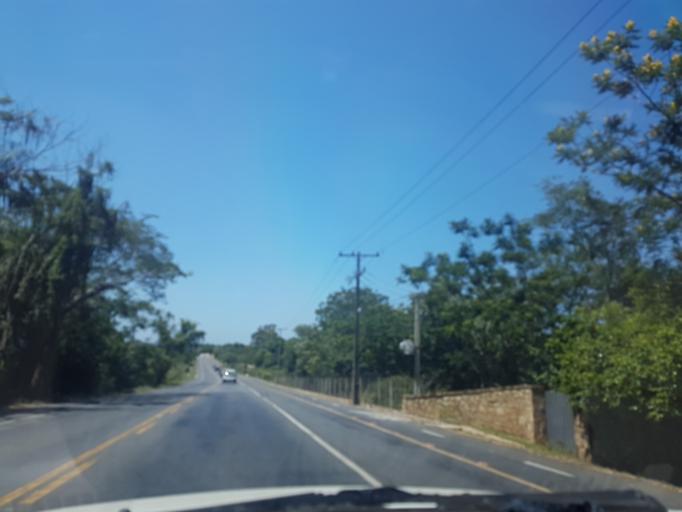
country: PY
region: Cordillera
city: San Bernardino
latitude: -25.2532
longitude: -57.3203
